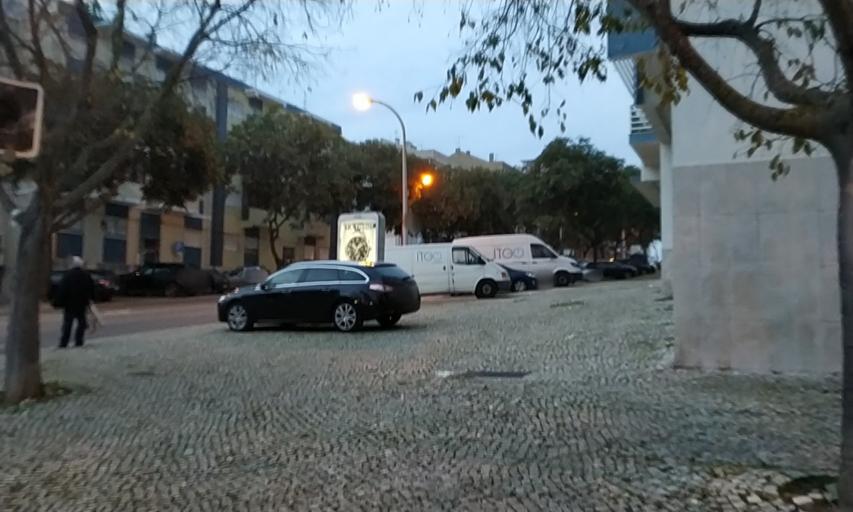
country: PT
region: Setubal
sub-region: Setubal
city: Setubal
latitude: 38.5227
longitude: -8.8748
